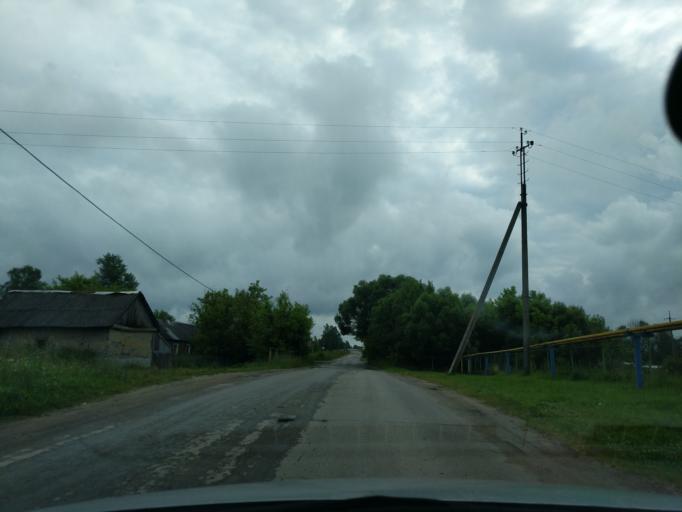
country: RU
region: Kaluga
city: Myatlevo
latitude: 54.7982
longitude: 35.7404
